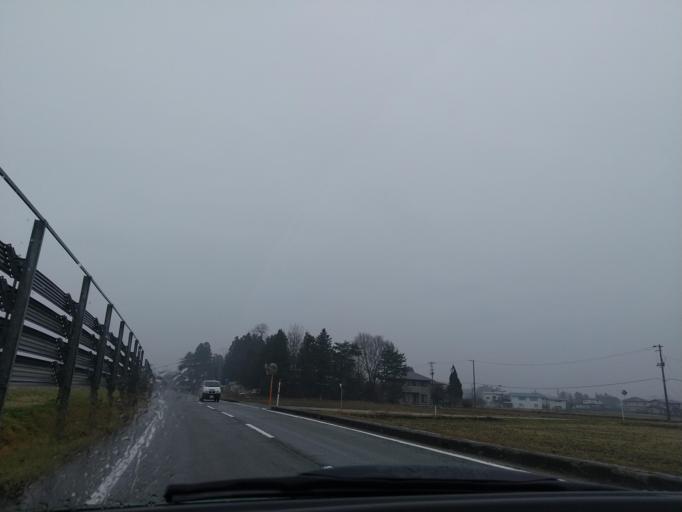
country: JP
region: Iwate
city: Morioka-shi
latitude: 39.6018
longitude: 141.1128
